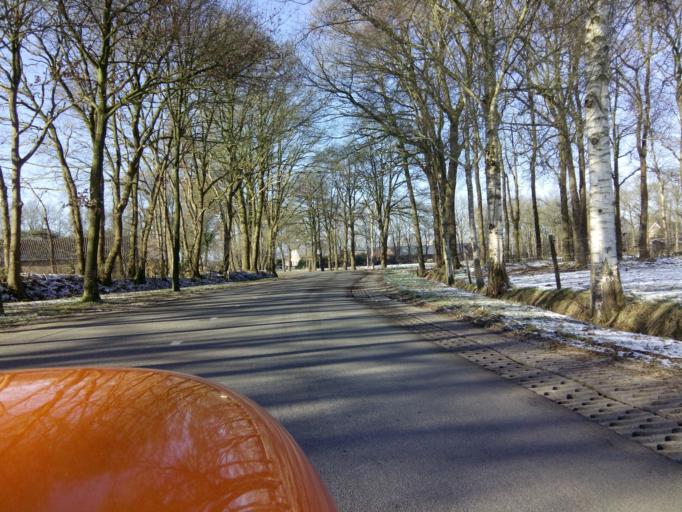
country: NL
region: Gelderland
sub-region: Gemeente Barneveld
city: Stroe
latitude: 52.1762
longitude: 5.6745
